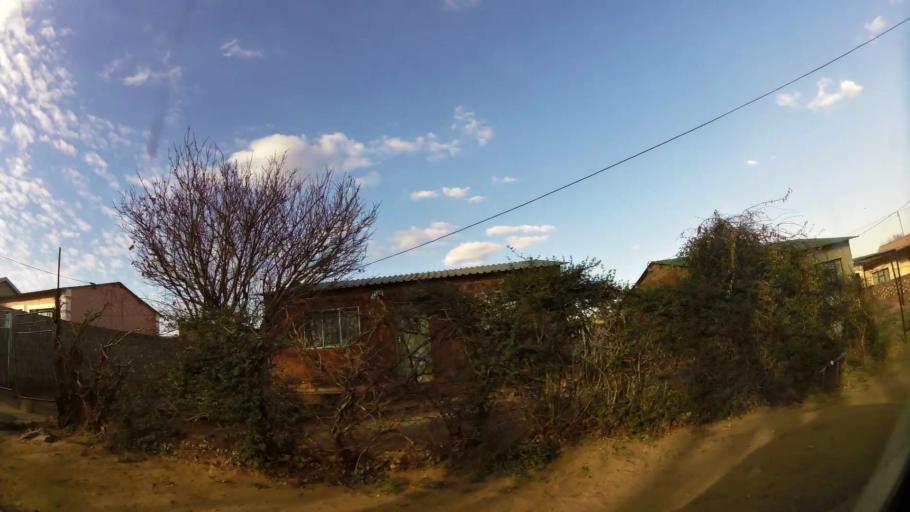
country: ZA
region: Gauteng
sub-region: City of Tshwane Metropolitan Municipality
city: Cullinan
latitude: -25.7070
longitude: 28.3796
